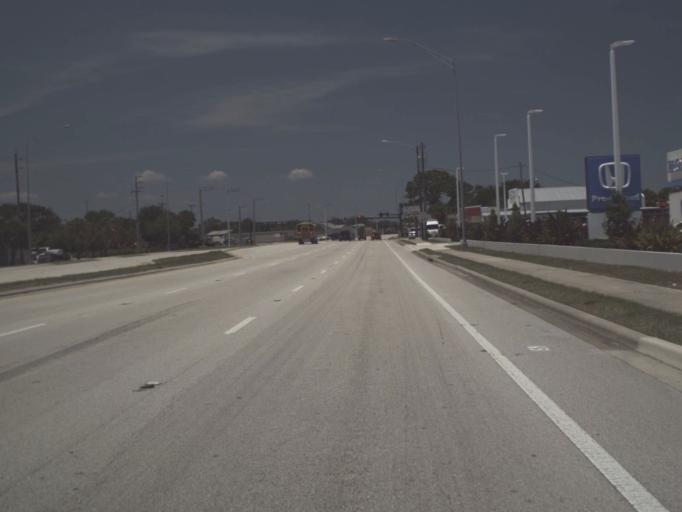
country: US
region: Florida
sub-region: Brevard County
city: Melbourne
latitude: 28.0620
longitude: -80.5949
